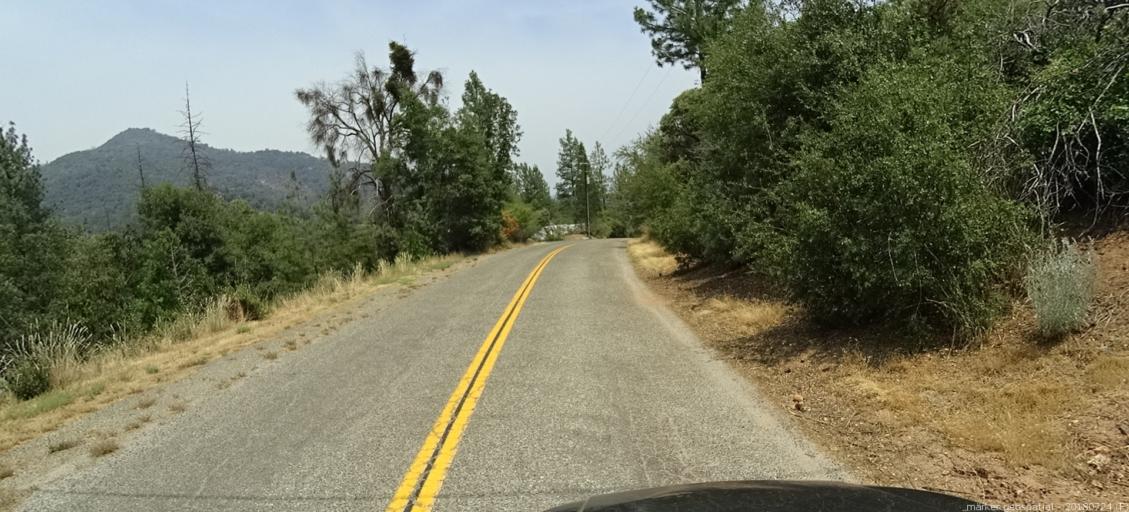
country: US
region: California
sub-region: Madera County
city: Oakhurst
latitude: 37.2473
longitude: -119.5564
